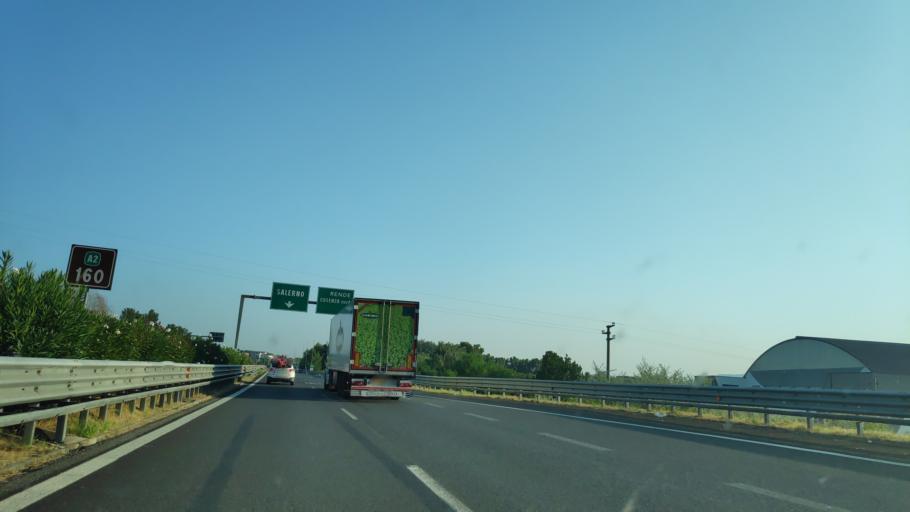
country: IT
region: Calabria
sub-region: Provincia di Cosenza
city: Quattromiglia
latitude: 39.3474
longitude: 16.2351
